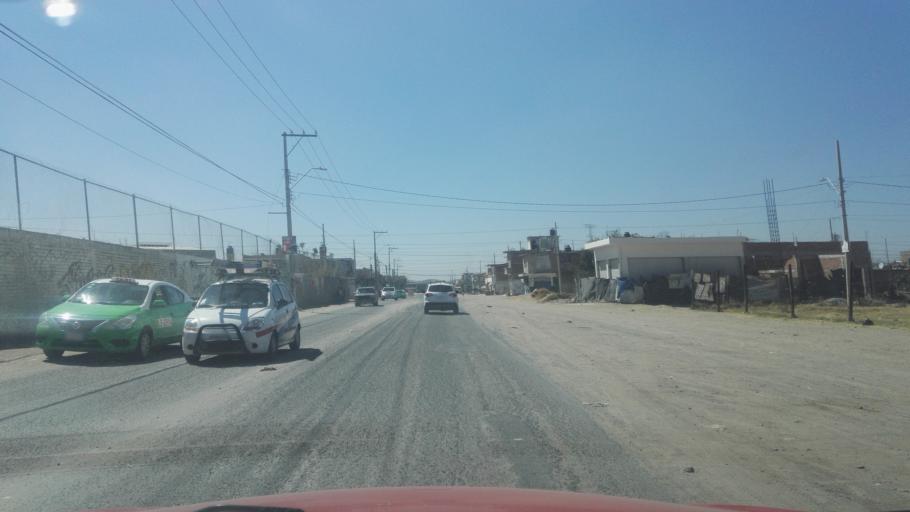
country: MX
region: Guanajuato
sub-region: Leon
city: Fraccionamiento Paraiso Real
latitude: 21.0931
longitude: -101.5922
